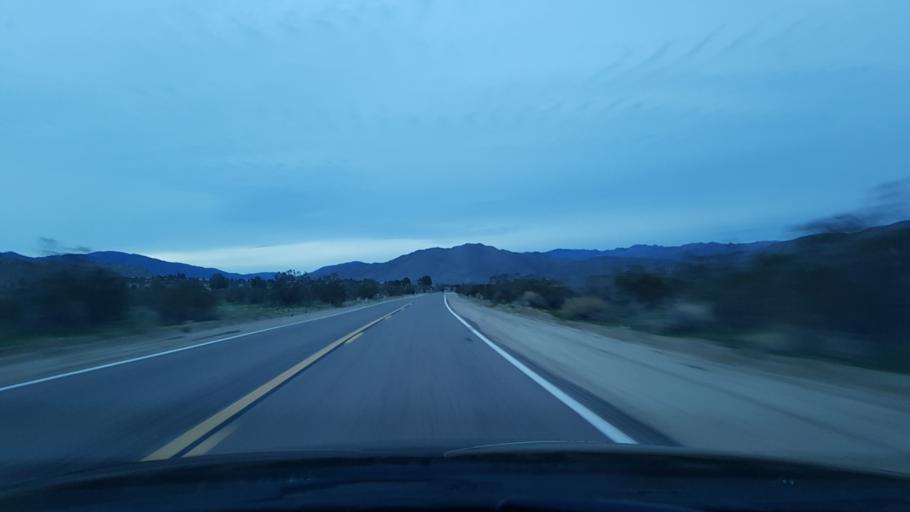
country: US
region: California
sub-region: San Diego County
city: Julian
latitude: 33.0541
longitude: -116.4192
